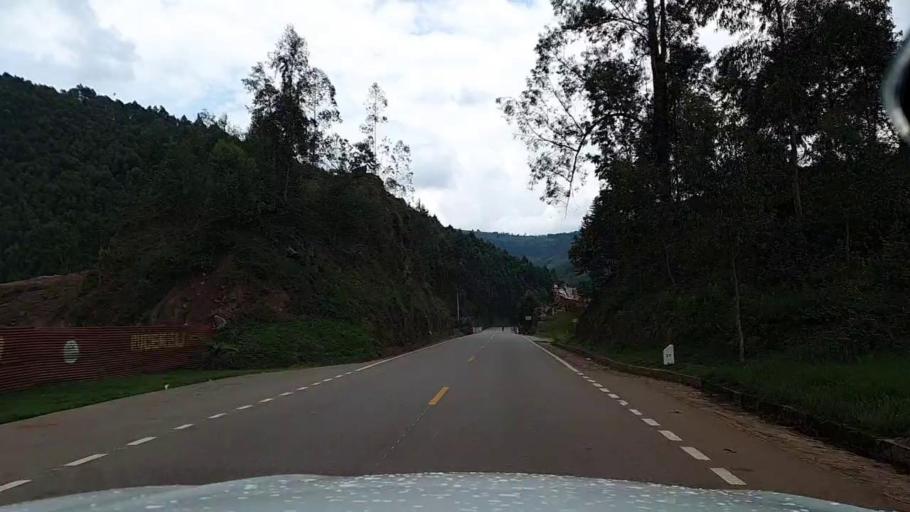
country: RW
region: Northern Province
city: Byumba
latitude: -1.7182
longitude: 30.1197
